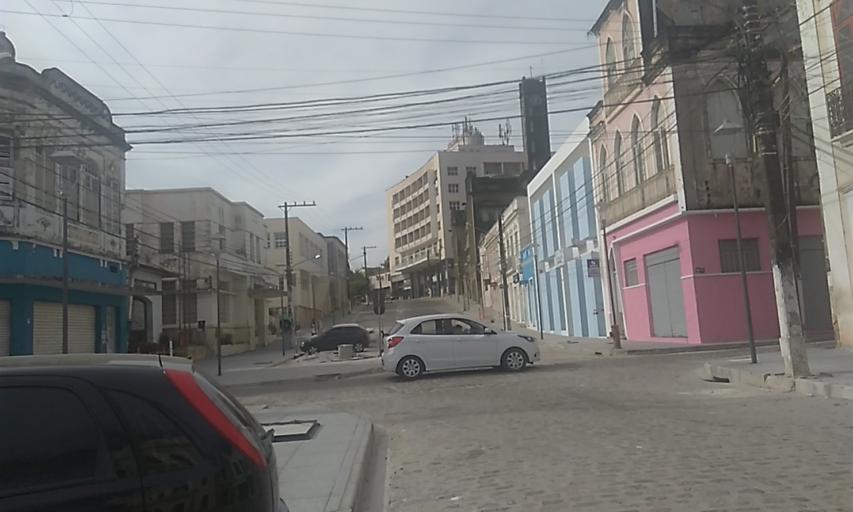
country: BR
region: Alagoas
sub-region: Penedo
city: Penedo
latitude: -10.2913
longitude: -36.5850
